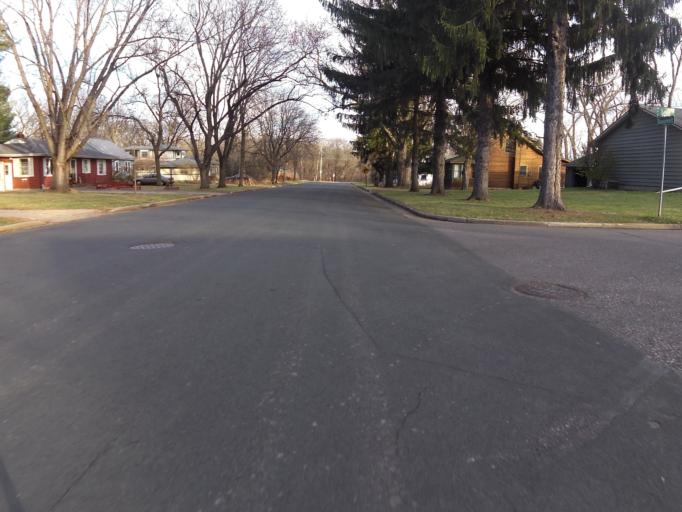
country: US
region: Wisconsin
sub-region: Pierce County
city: River Falls
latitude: 44.8647
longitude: -92.6282
